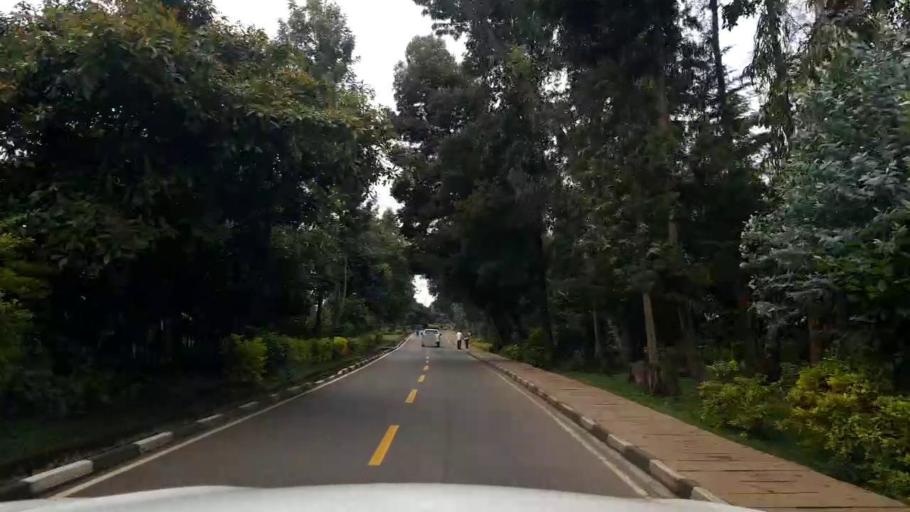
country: RW
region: Northern Province
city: Musanze
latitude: -1.4515
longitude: 29.5958
